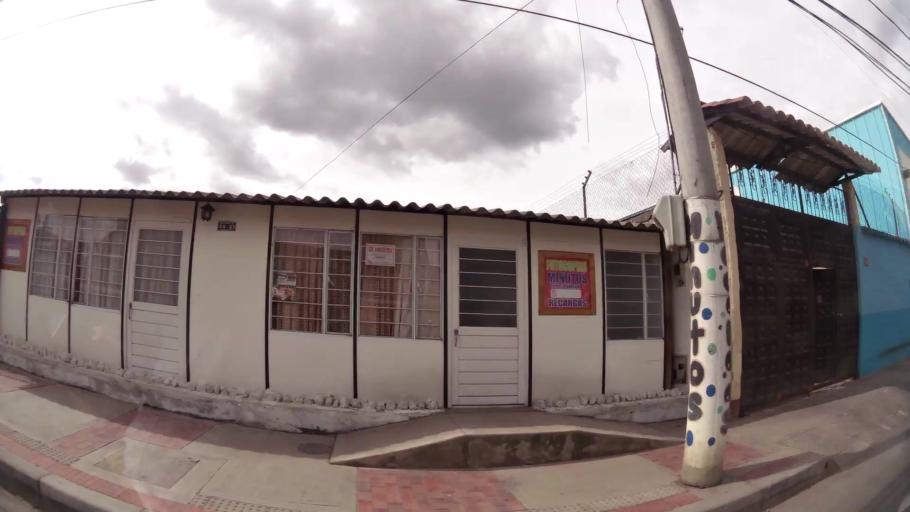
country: CO
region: Cundinamarca
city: Funza
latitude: 4.7126
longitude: -74.2003
